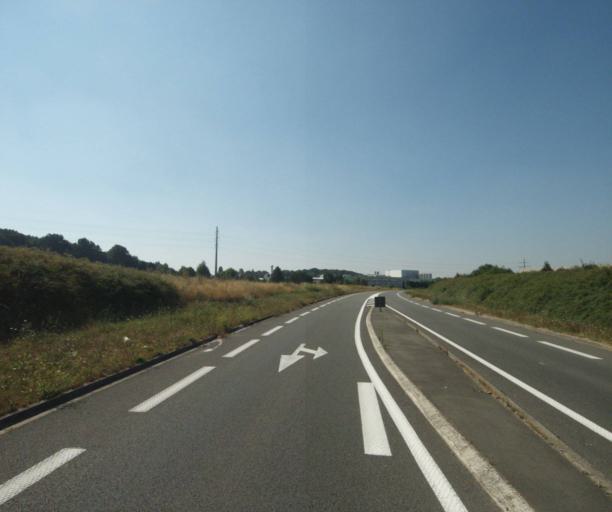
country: FR
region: Nord-Pas-de-Calais
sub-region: Departement du Nord
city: Bousbecque
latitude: 50.7693
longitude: 3.0919
